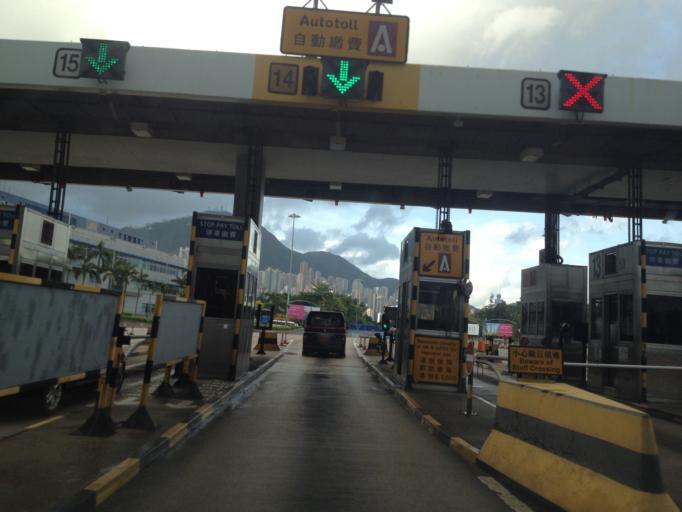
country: HK
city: Hong Kong
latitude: 22.3036
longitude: 114.1589
